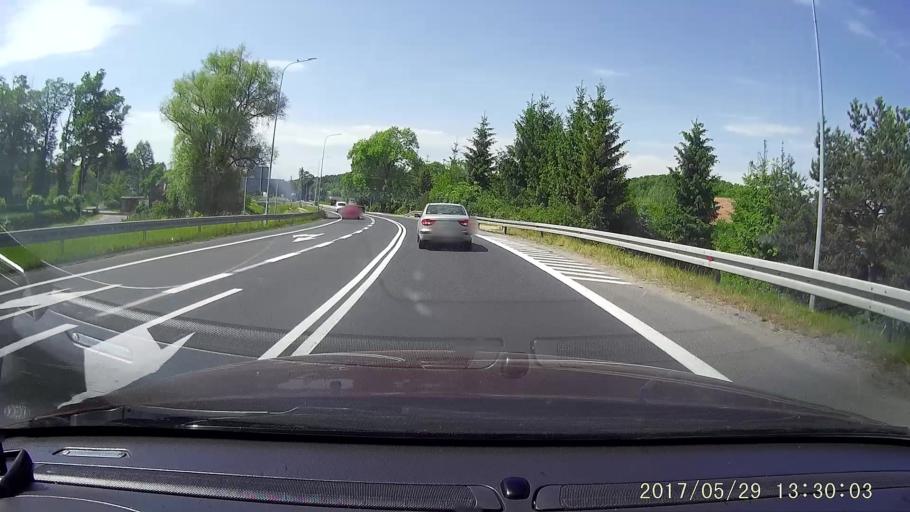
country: PL
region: Lower Silesian Voivodeship
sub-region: Powiat lubanski
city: Olszyna
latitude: 51.0747
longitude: 15.3601
